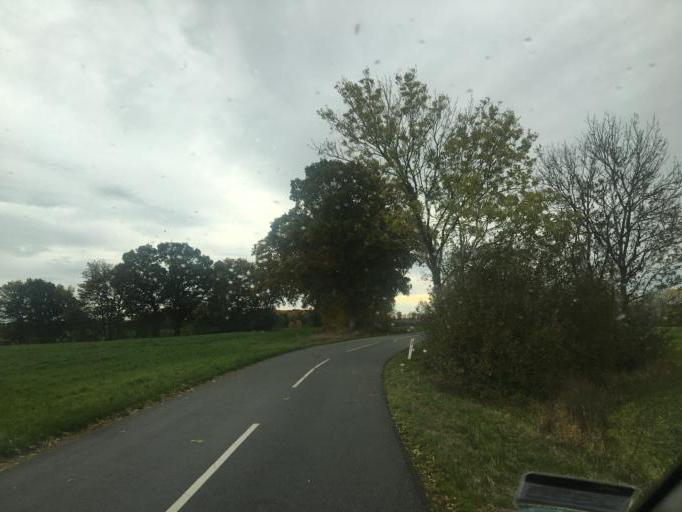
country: DK
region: Zealand
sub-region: Koge Kommune
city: Bjaeverskov
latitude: 55.4126
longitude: 11.9837
